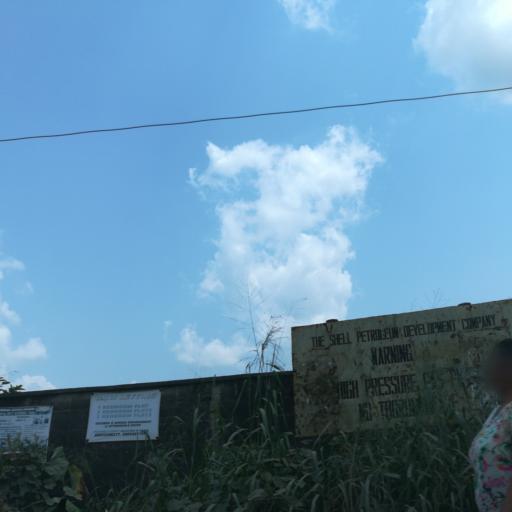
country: NG
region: Rivers
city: Okrika
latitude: 4.8949
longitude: 7.1217
